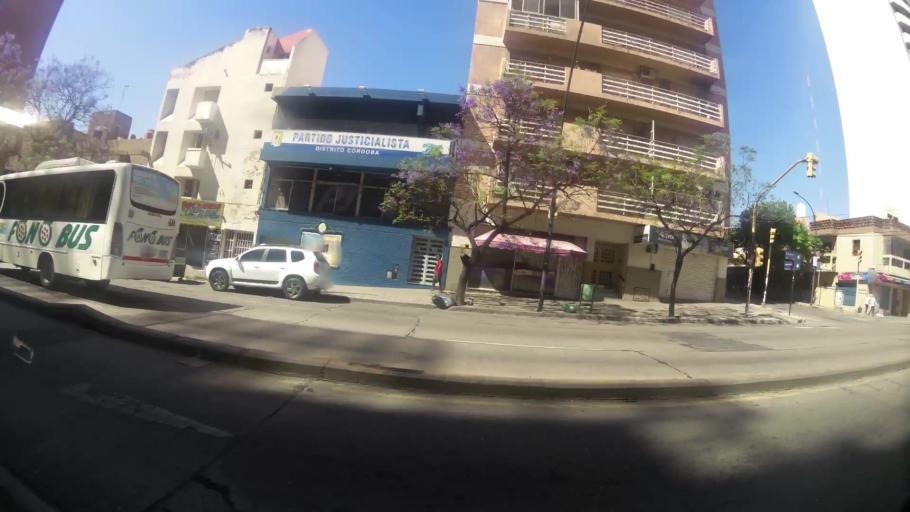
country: AR
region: Cordoba
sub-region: Departamento de Capital
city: Cordoba
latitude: -31.4174
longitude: -64.1940
